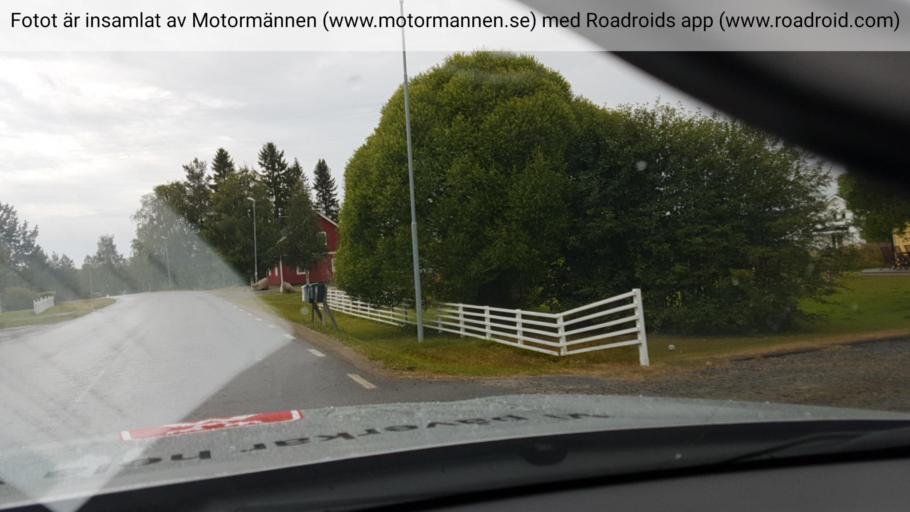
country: SE
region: Norrbotten
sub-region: Bodens Kommun
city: Boden
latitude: 65.9036
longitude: 21.3137
